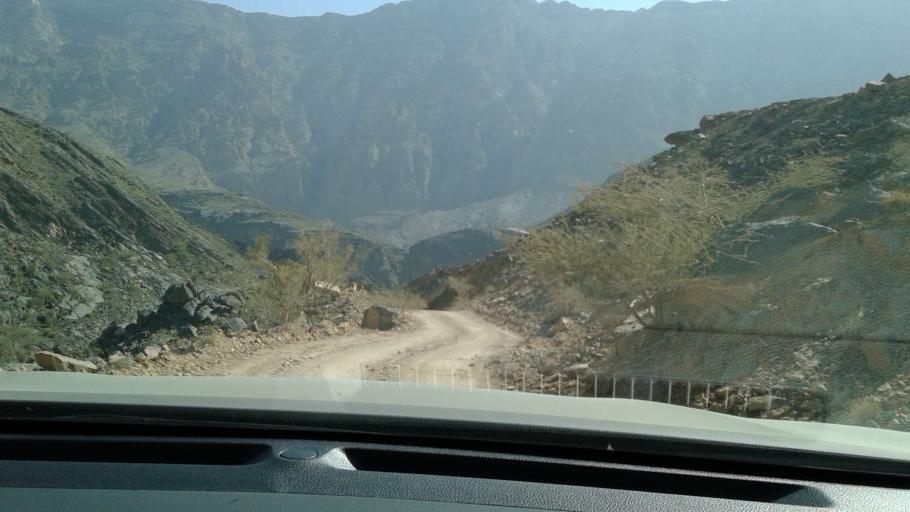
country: OM
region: Al Batinah
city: Bayt al `Awabi
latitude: 23.2035
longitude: 57.3917
